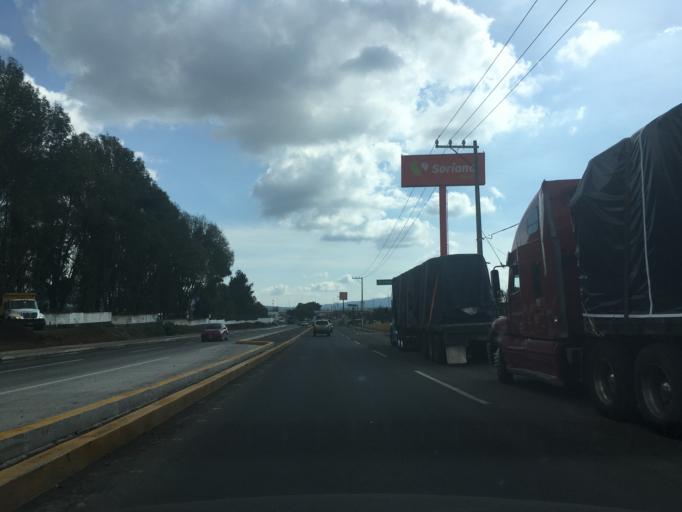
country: MX
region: Michoacan
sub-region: Uruapan
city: Toreo Bajo (El Toreo Bajo)
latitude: 19.4273
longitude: -102.0252
